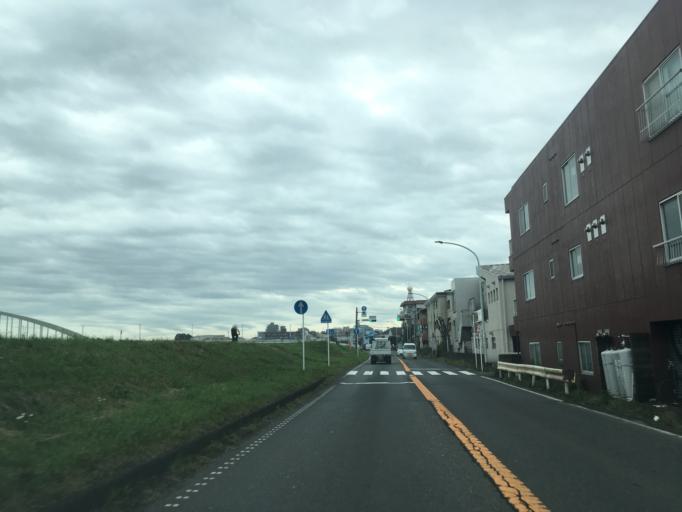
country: JP
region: Tokyo
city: Chofugaoka
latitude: 35.6267
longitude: 139.5654
